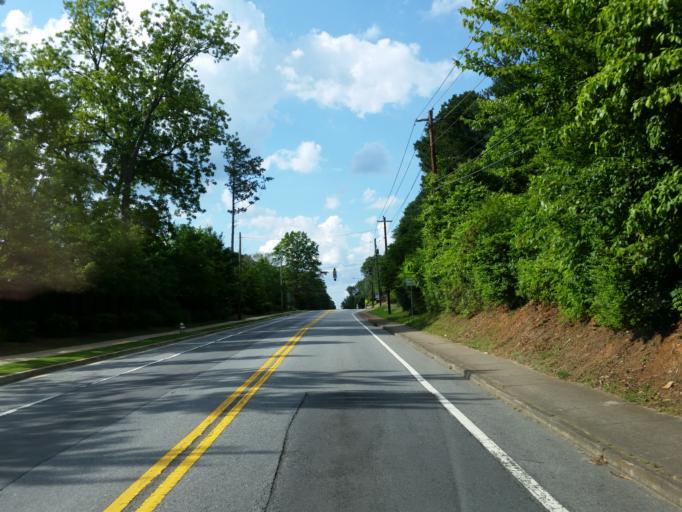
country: US
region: Georgia
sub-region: Fulton County
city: Roswell
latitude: 34.0365
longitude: -84.3613
